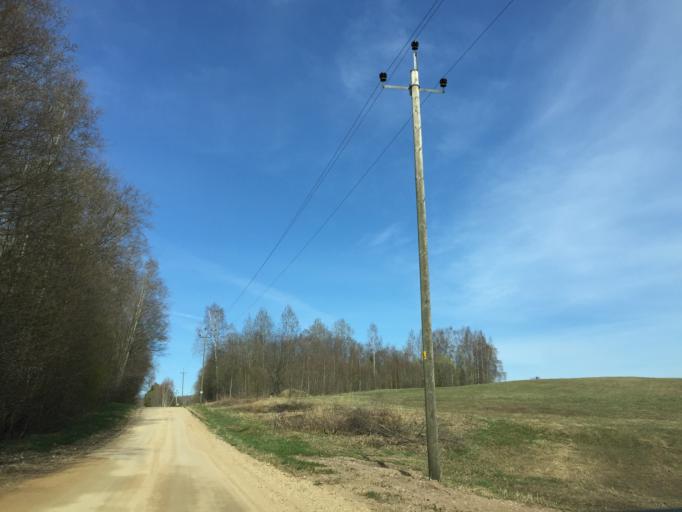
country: EE
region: Vorumaa
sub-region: Antsla vald
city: Vana-Antsla
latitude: 57.9637
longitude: 26.3417
